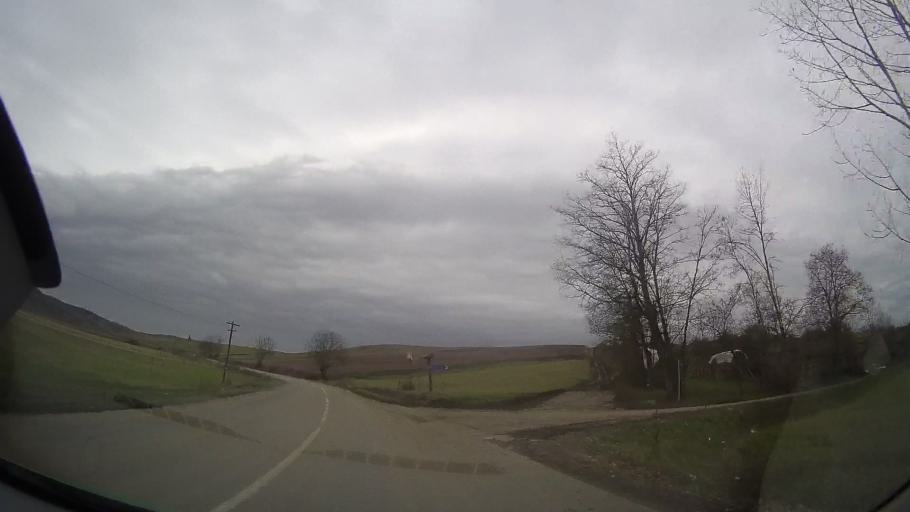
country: RO
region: Bistrita-Nasaud
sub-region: Comuna Milas
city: Milas
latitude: 46.7935
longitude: 24.4212
